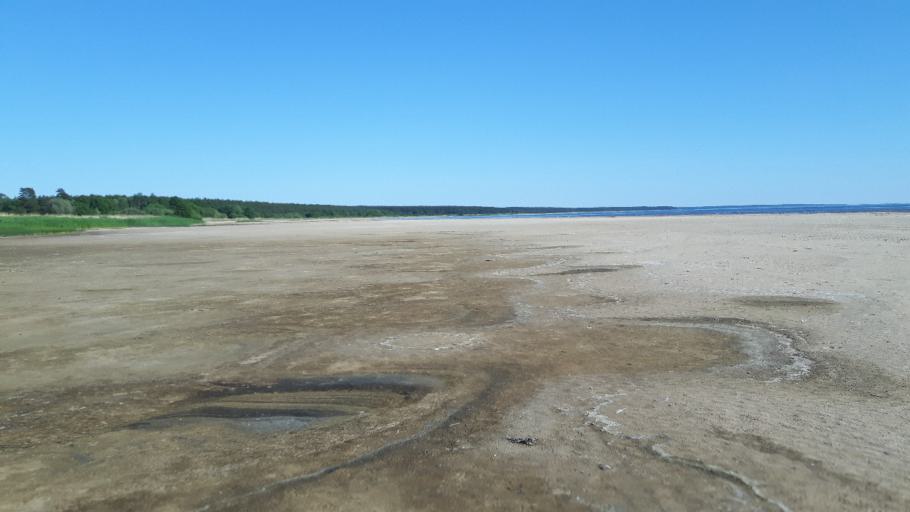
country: LV
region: Salacgrivas
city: Salacgriva
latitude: 57.6980
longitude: 24.3437
